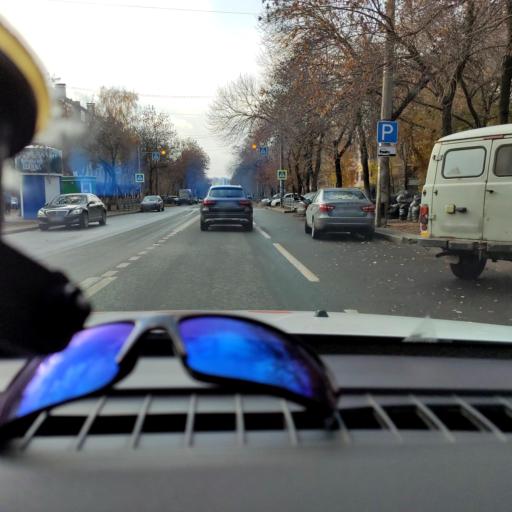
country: RU
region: Samara
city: Samara
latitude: 53.1964
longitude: 50.1673
